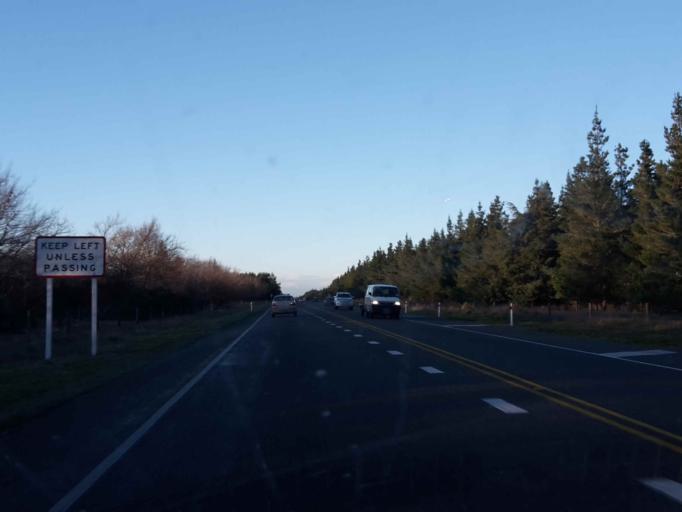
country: NZ
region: Canterbury
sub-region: Selwyn District
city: Burnham
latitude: -43.6105
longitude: 172.3272
